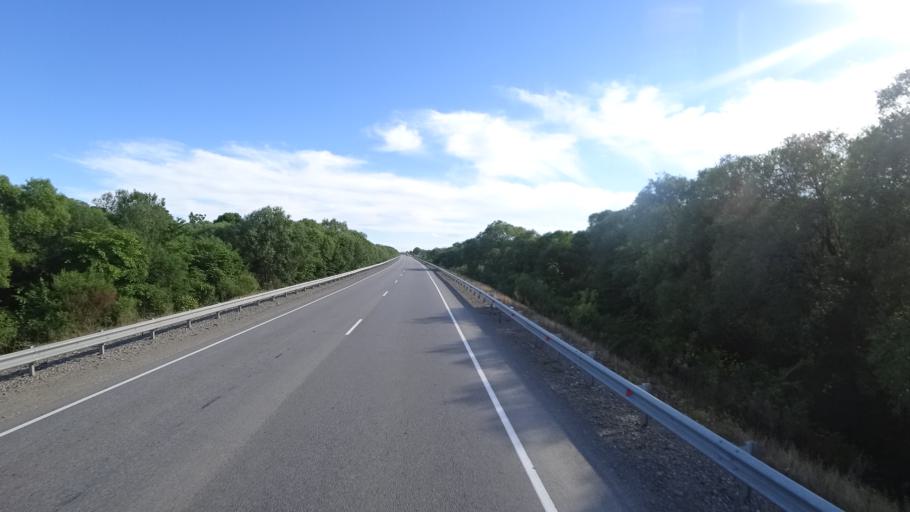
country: RU
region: Khabarovsk Krai
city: Khor
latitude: 47.8813
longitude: 134.9709
